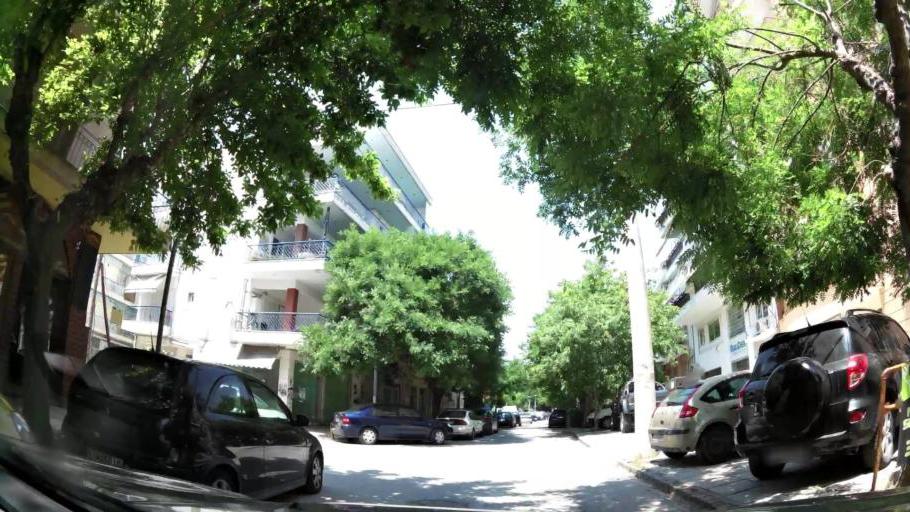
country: GR
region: Central Macedonia
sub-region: Nomos Thessalonikis
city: Thessaloniki
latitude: 40.6462
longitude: 22.9311
